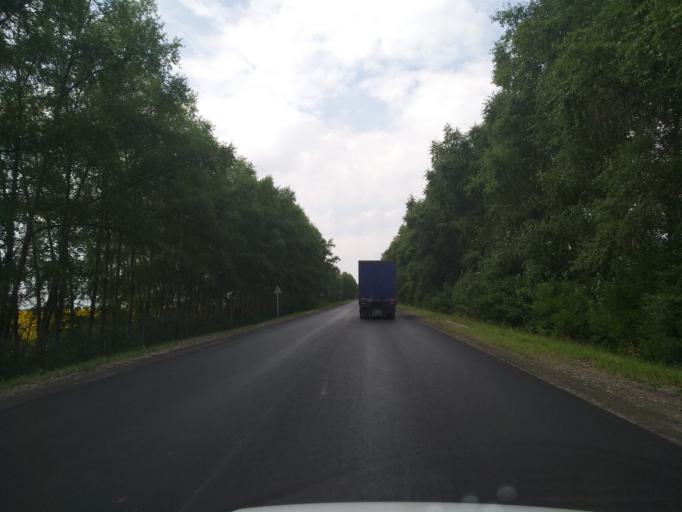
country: RU
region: Voronezj
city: Pereleshino
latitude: 51.7376
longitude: 40.0805
